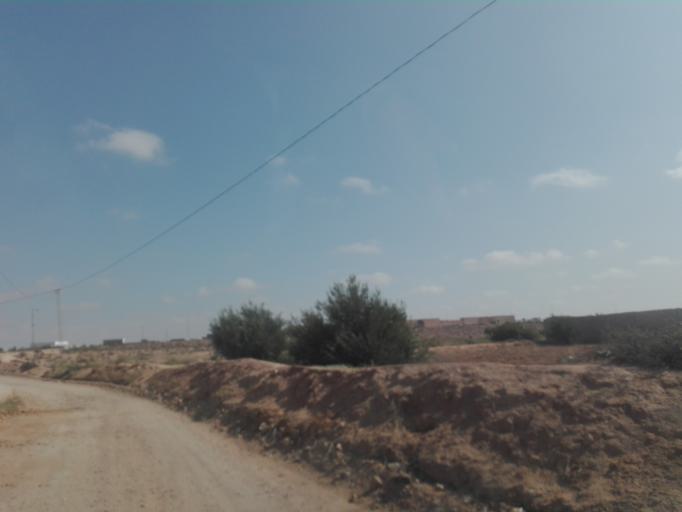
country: TN
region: Madanin
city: Medenine
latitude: 33.4278
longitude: 10.4057
